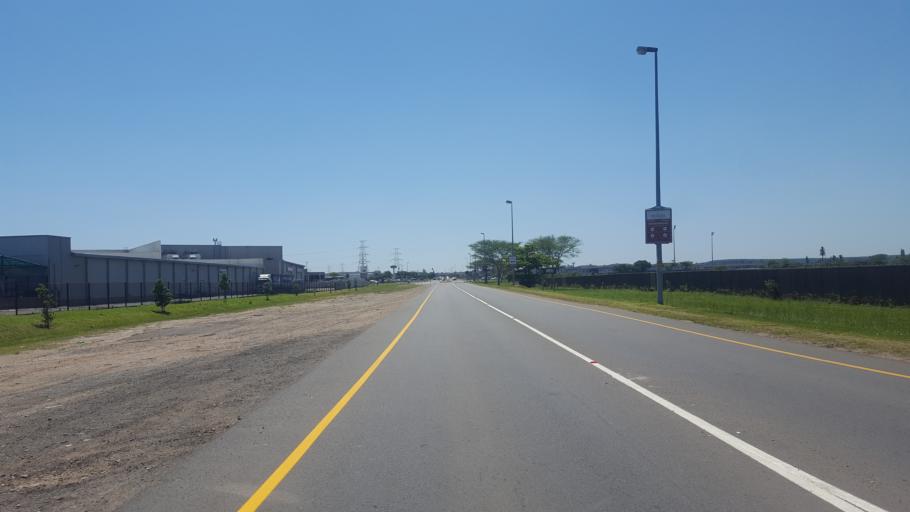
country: ZA
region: KwaZulu-Natal
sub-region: uThungulu District Municipality
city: Richards Bay
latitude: -28.7473
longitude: 32.0529
